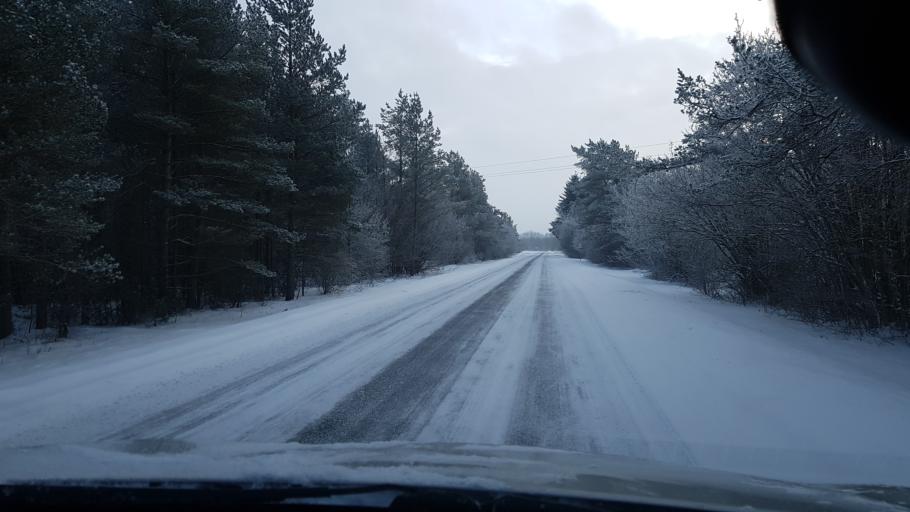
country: EE
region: Harju
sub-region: Keila linn
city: Keila
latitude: 59.3701
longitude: 24.4068
